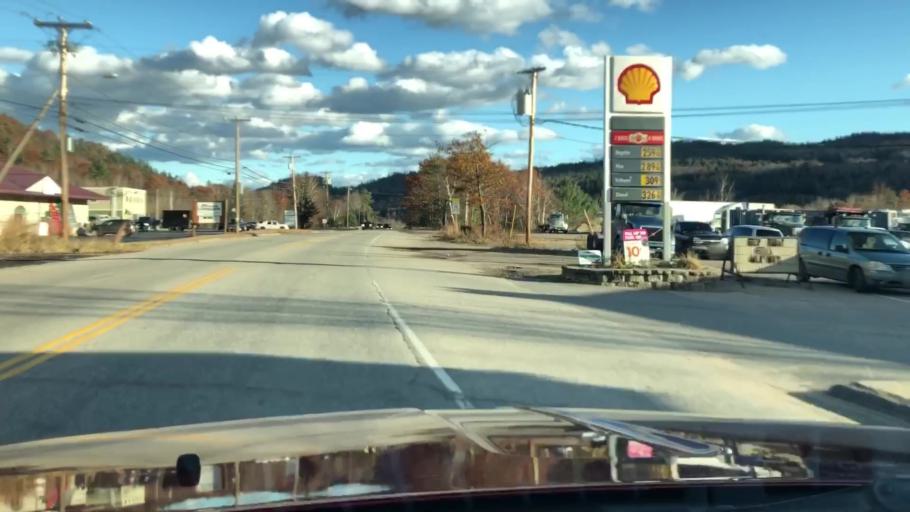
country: US
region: Maine
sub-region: Oxford County
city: Mexico
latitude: 44.5358
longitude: -70.5089
